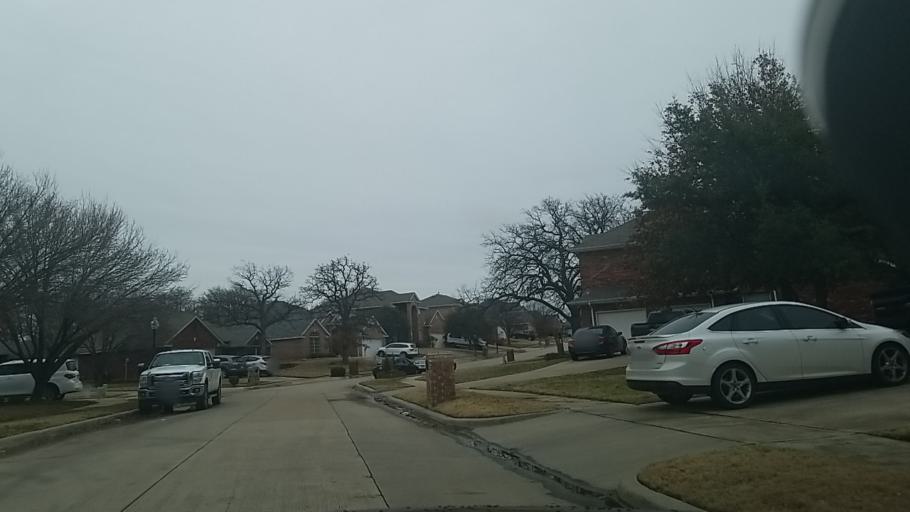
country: US
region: Texas
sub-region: Denton County
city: Corinth
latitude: 33.1560
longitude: -97.0691
